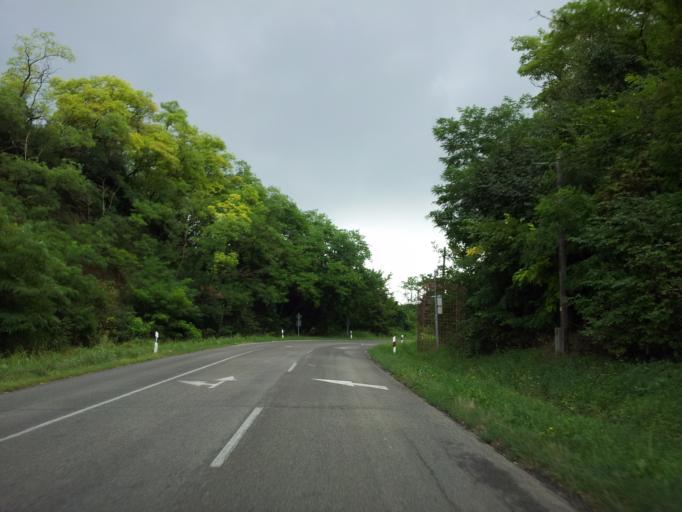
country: HU
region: Tolna
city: Hogyesz
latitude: 46.5106
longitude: 18.4055
